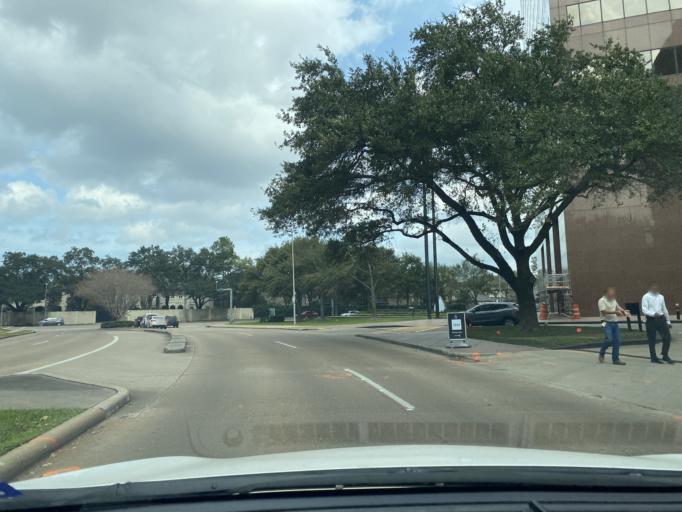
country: US
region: Texas
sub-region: Harris County
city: Hunters Creek Village
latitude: 29.7492
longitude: -95.4728
